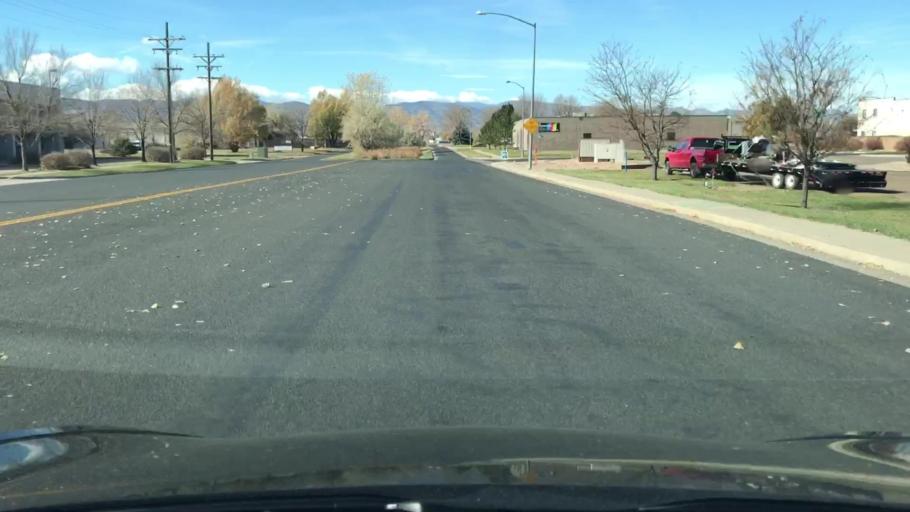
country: US
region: Colorado
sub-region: Larimer County
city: Fort Collins
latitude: 40.5881
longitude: -105.0307
